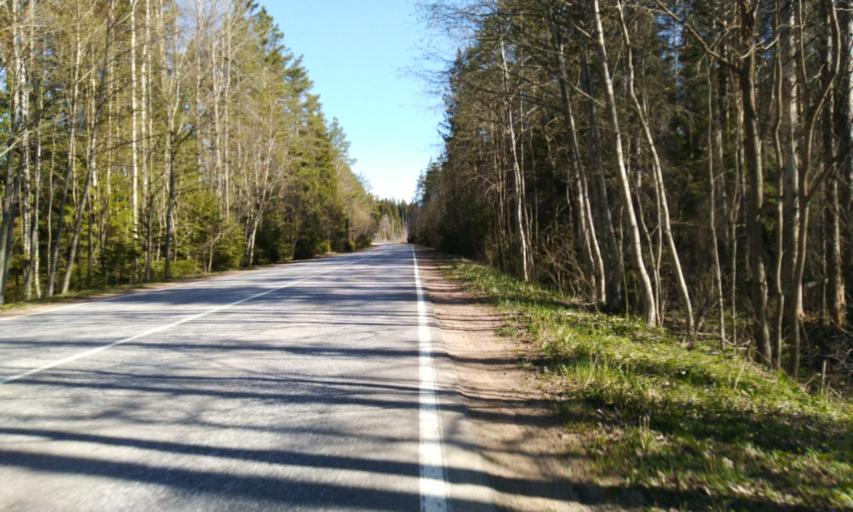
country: RU
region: Leningrad
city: Garbolovo
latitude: 60.3575
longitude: 30.4449
